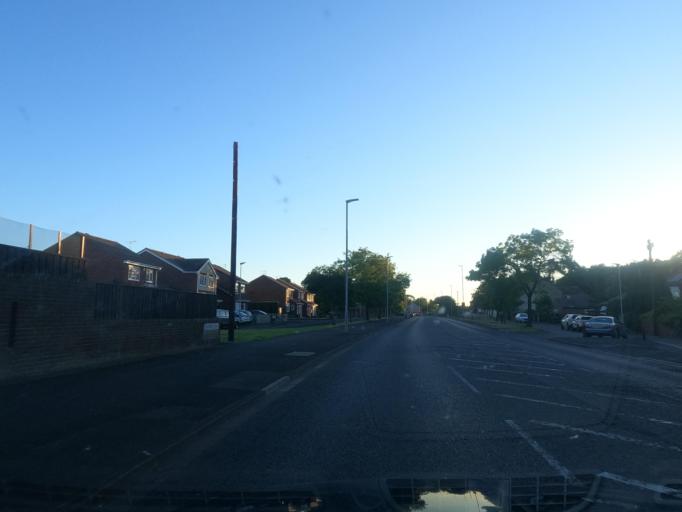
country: GB
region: England
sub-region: Northumberland
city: Blyth
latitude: 55.1304
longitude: -1.5393
